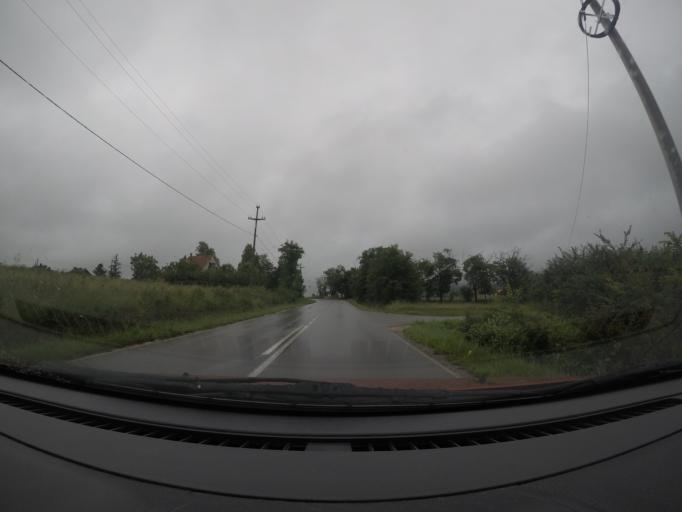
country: RS
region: Central Serbia
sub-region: Belgrade
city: Sopot
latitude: 44.4844
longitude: 20.5559
